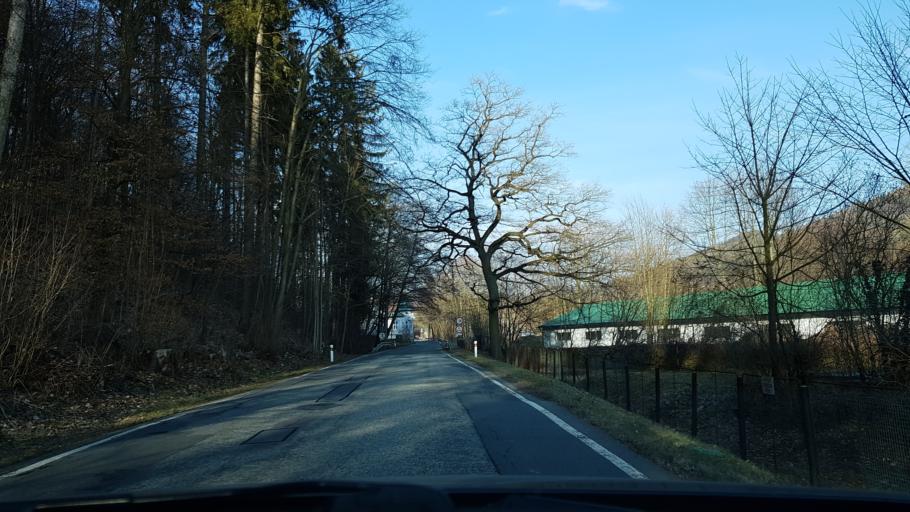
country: CZ
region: Olomoucky
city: Dolni Bohdikov
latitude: 50.0251
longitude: 16.8973
